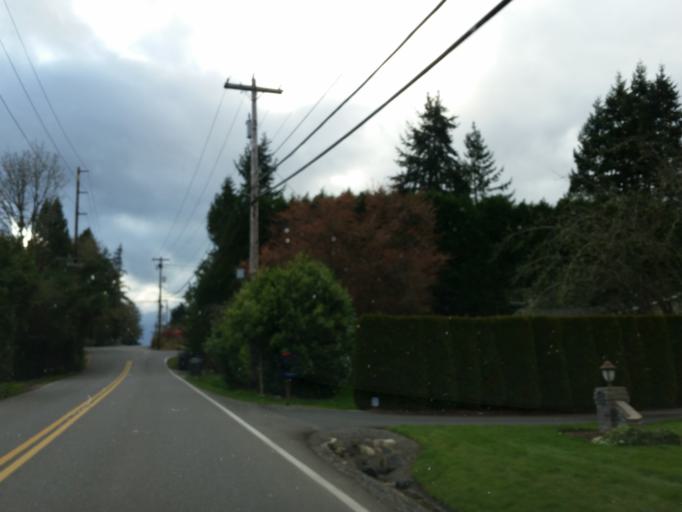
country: US
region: Washington
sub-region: King County
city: Woodinville
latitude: 47.7762
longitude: -122.1682
